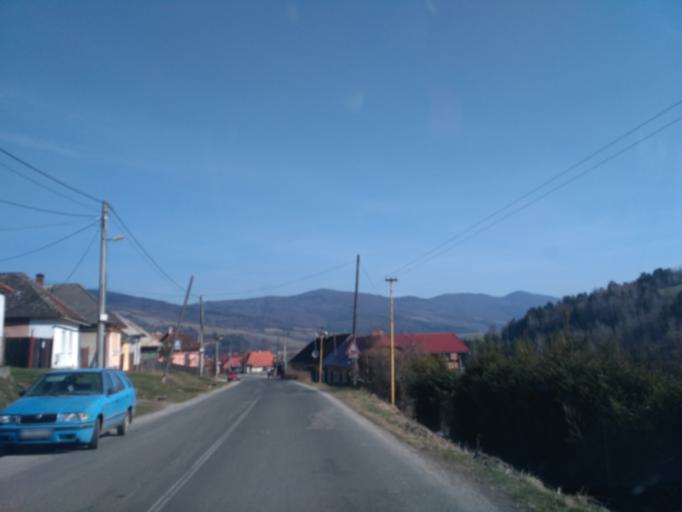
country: SK
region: Kosicky
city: Medzev
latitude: 48.7967
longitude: 20.8069
